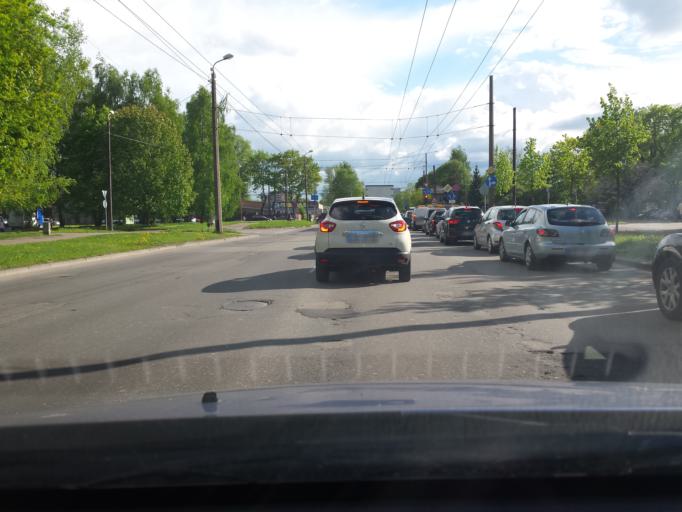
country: LV
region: Riga
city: Riga
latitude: 56.9519
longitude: 24.1741
